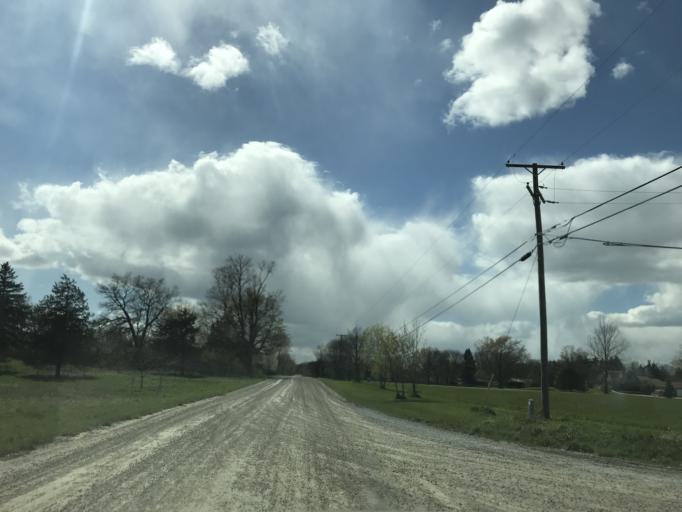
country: US
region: Michigan
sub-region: Livingston County
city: Whitmore Lake
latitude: 42.4037
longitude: -83.6941
